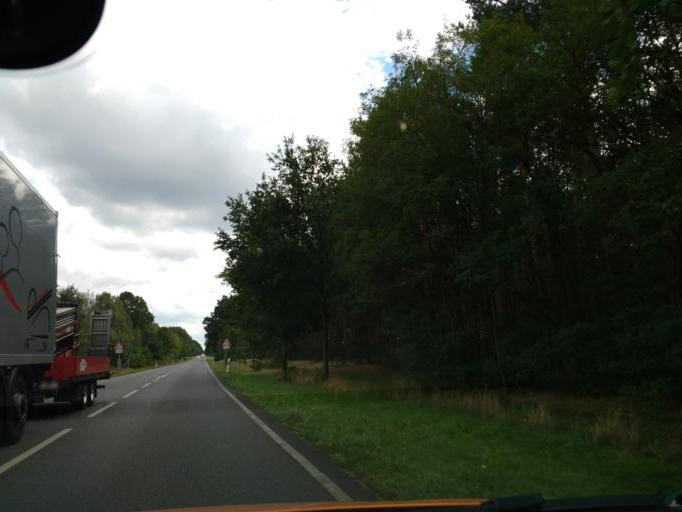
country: DE
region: Brandenburg
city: Marienwerder
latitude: 52.8569
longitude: 13.5497
